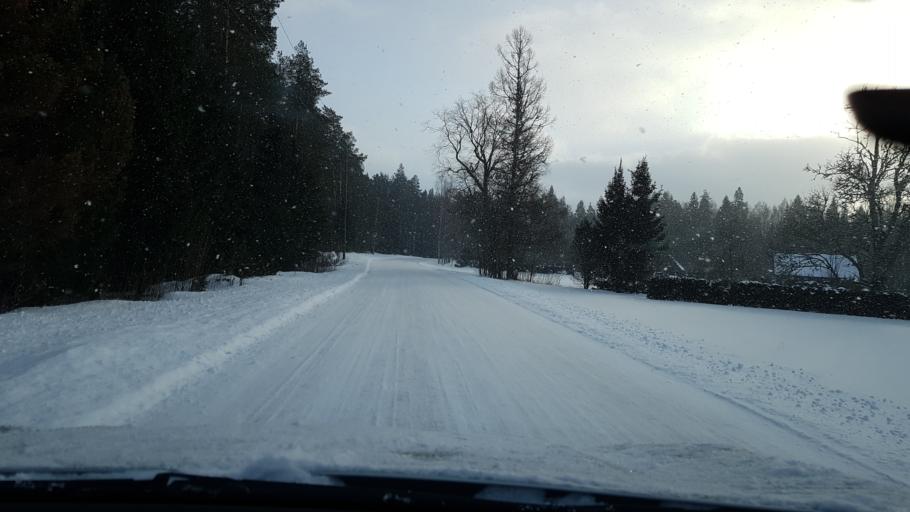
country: EE
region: Harju
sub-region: Nissi vald
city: Turba
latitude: 59.1876
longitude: 24.1394
